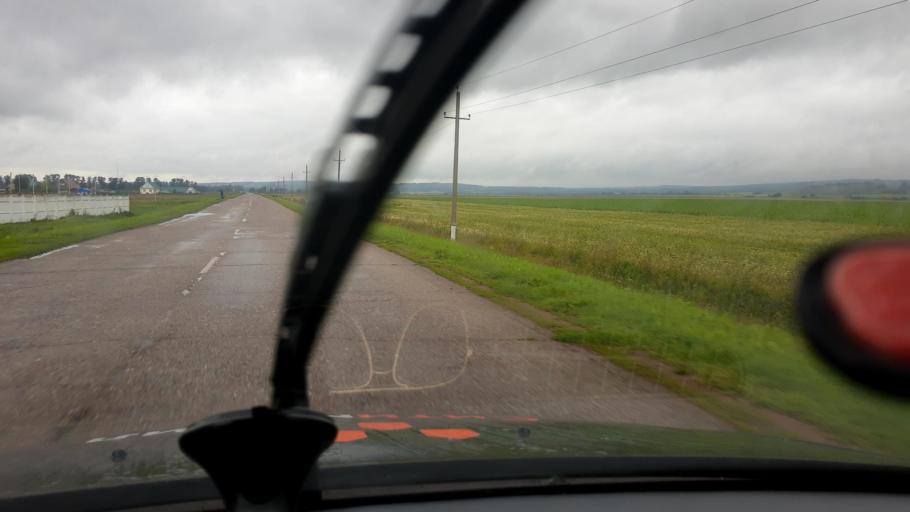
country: RU
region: Bashkortostan
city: Karmaskaly
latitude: 53.9878
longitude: 56.3973
